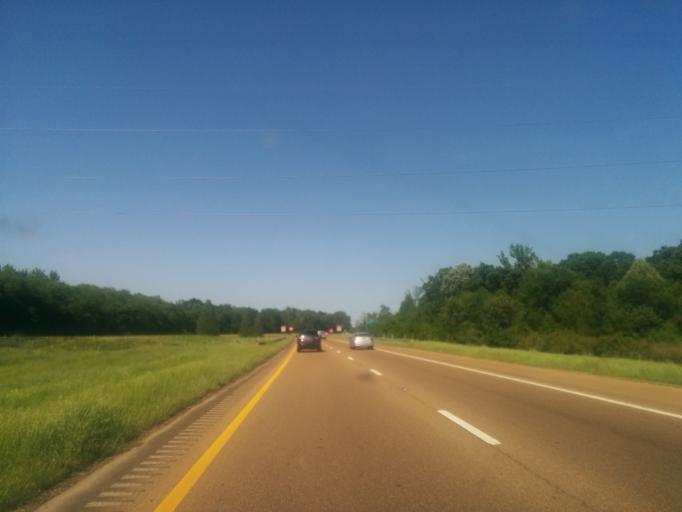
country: US
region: Mississippi
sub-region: Madison County
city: Madison
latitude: 32.5019
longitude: -90.1188
